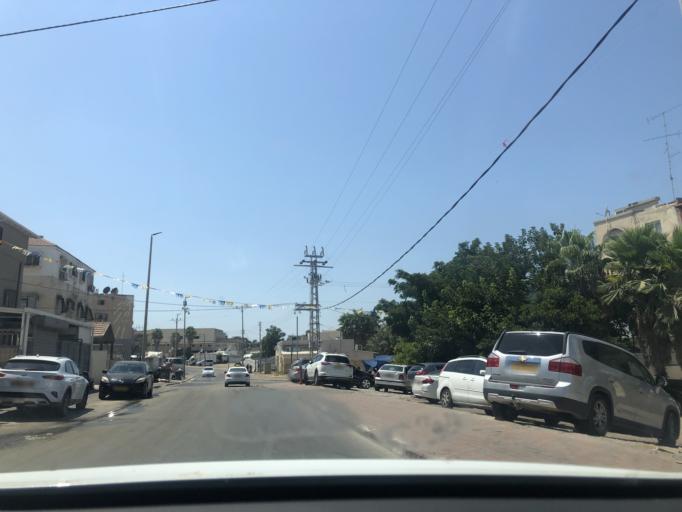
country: IL
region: Central District
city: Lod
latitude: 31.9565
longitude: 34.9027
